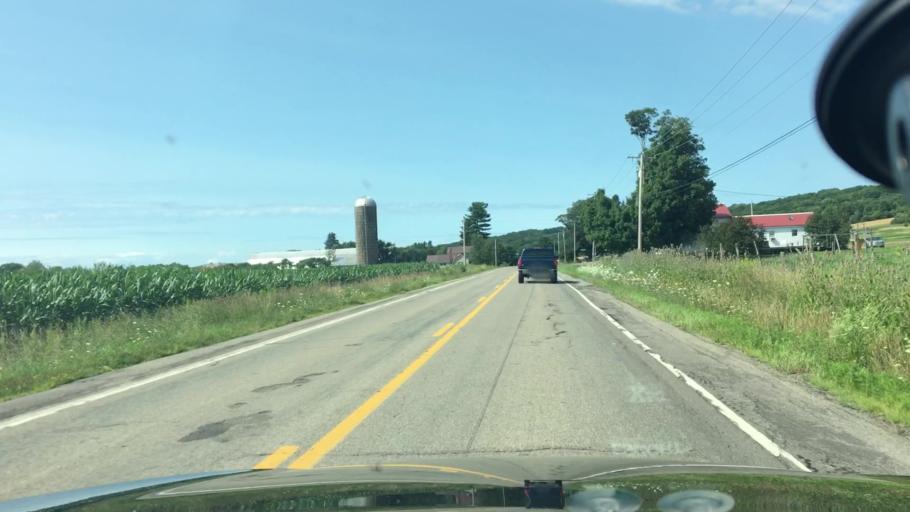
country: US
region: New York
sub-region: Chautauqua County
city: Brocton
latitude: 42.3036
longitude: -79.3531
